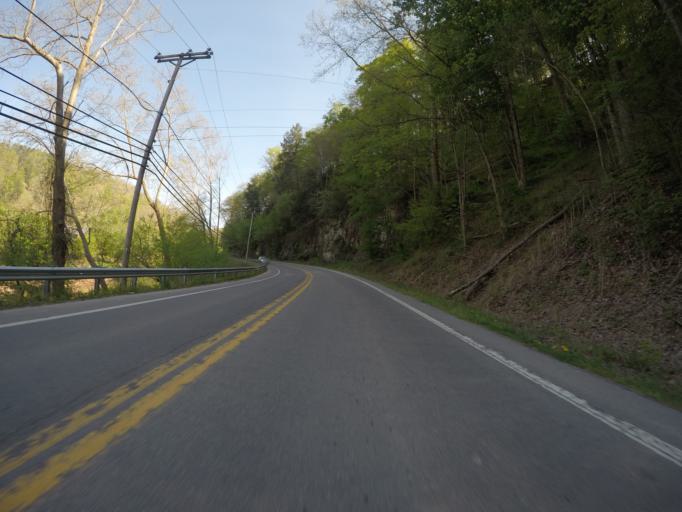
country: US
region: West Virginia
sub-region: Kanawha County
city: Clendenin
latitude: 38.4934
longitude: -81.3536
